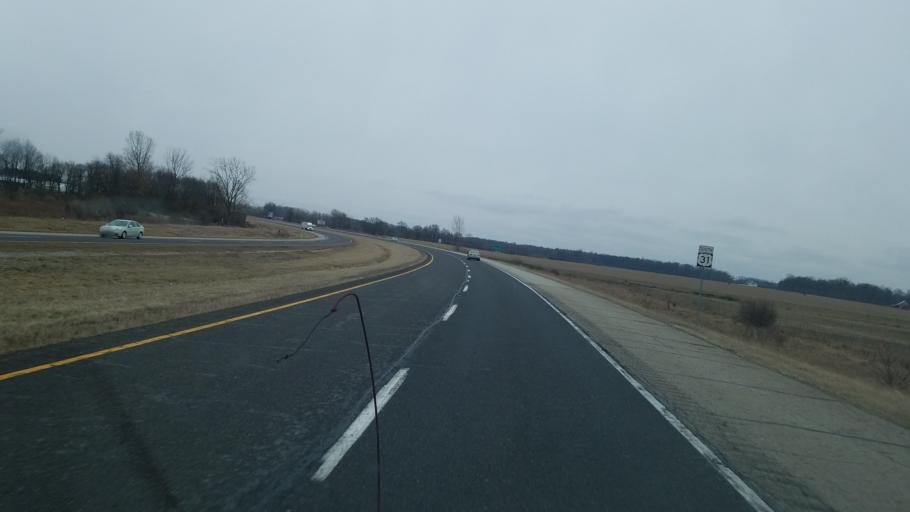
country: US
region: Indiana
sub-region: Fulton County
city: Rochester
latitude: 41.0540
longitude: -86.2398
